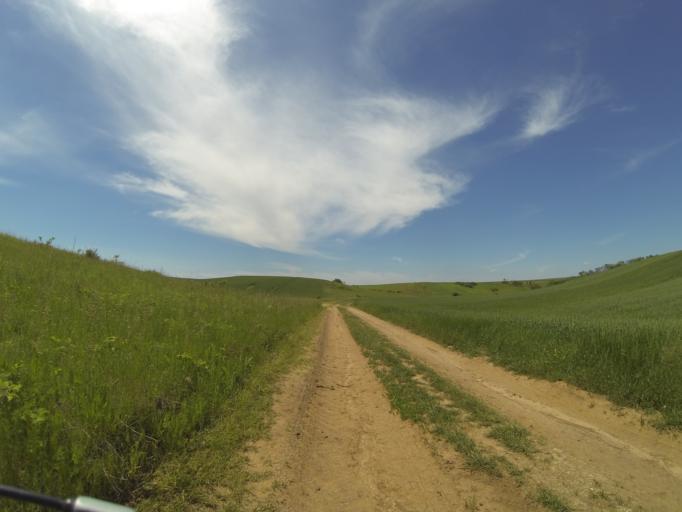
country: RO
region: Dolj
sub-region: Comuna Teslui
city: Teslui
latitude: 44.1925
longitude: 24.1450
